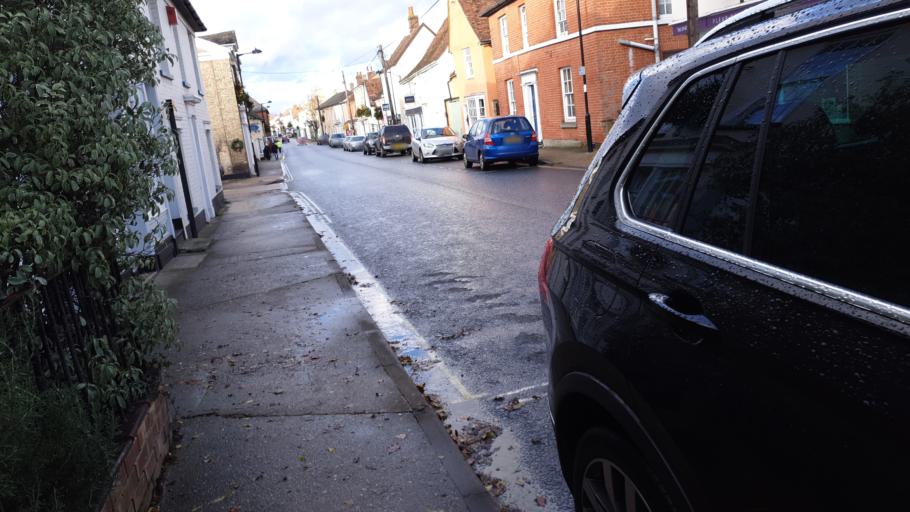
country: GB
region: England
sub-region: Suffolk
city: Hadleigh
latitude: 52.0416
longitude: 0.9555
